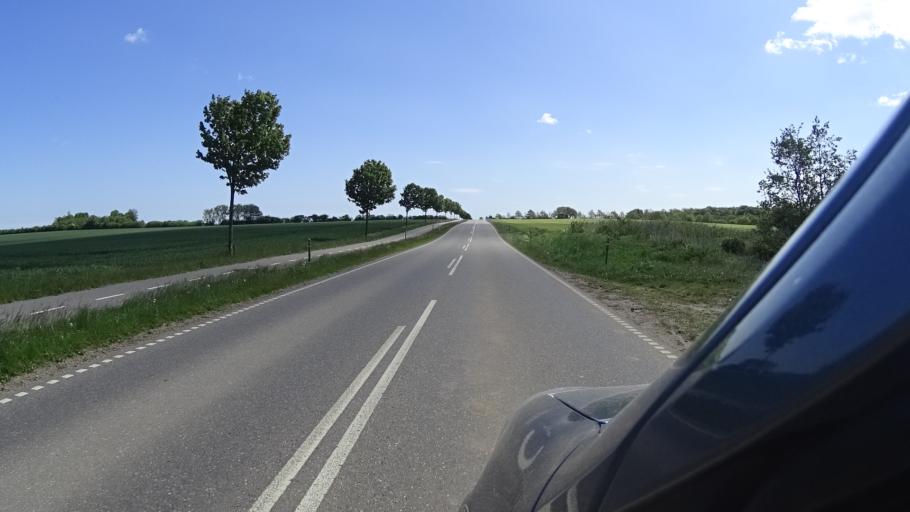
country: DK
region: South Denmark
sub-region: Vejle Kommune
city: Borkop
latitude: 55.6371
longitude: 9.6179
